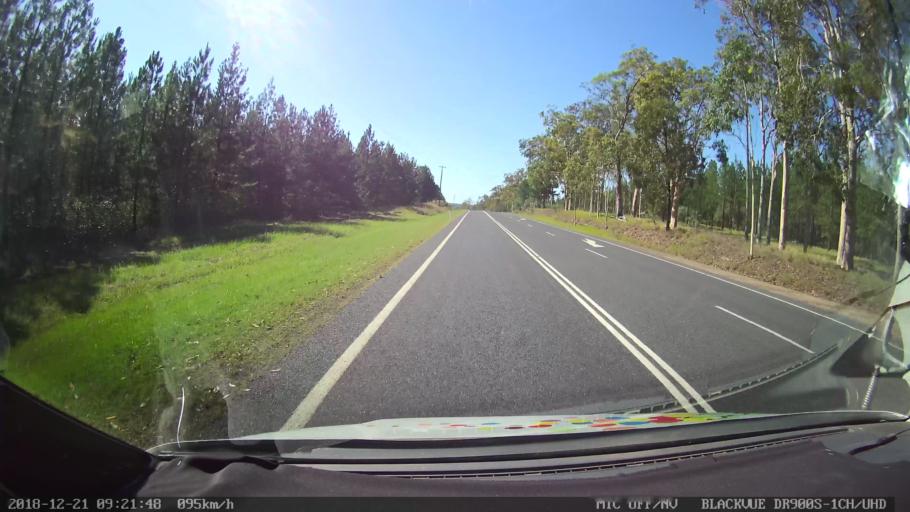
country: AU
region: New South Wales
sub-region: Clarence Valley
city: Maclean
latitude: -29.3338
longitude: 153.0004
